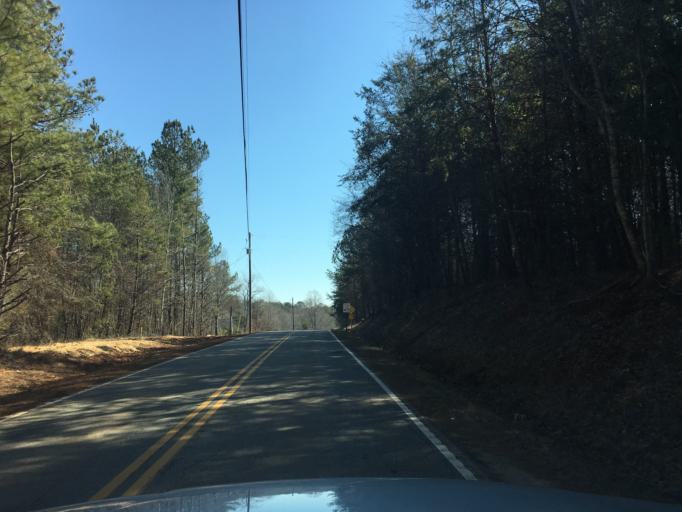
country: US
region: South Carolina
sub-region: Pickens County
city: Liberty
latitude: 34.7962
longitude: -82.7343
